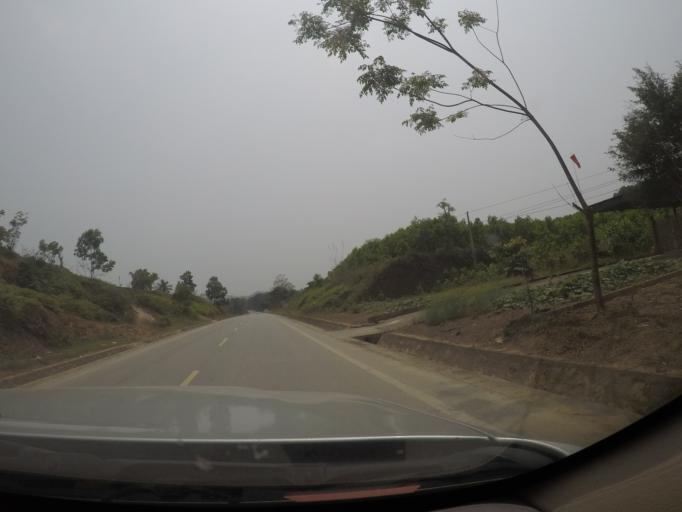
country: VN
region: Thanh Hoa
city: Thi Tran Yen Cat
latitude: 19.6989
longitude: 105.4525
